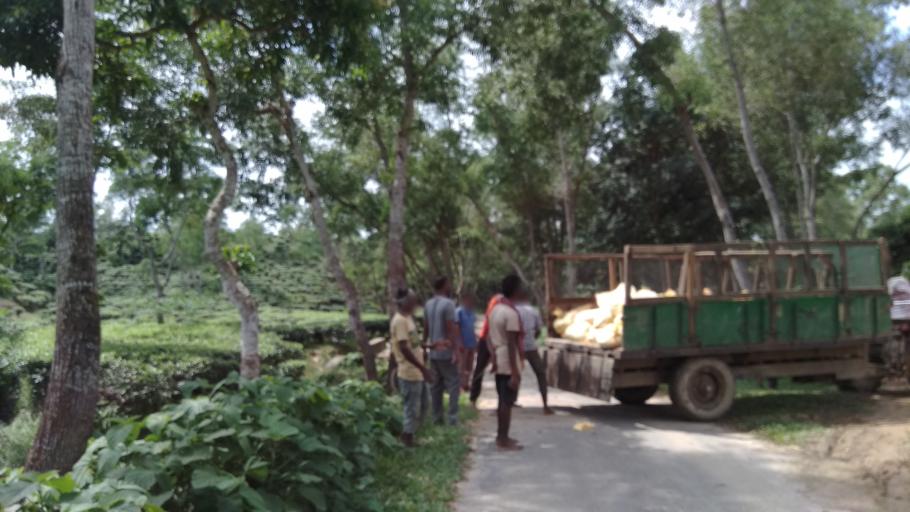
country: IN
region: Tripura
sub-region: Dhalai
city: Kamalpur
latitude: 24.3024
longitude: 91.8177
